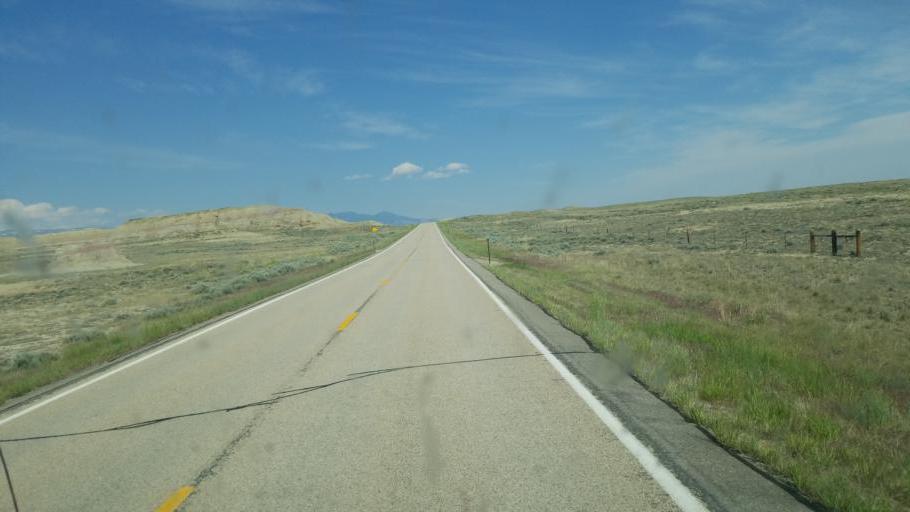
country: US
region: Wyoming
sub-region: Park County
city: Powell
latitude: 44.8363
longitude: -108.9842
